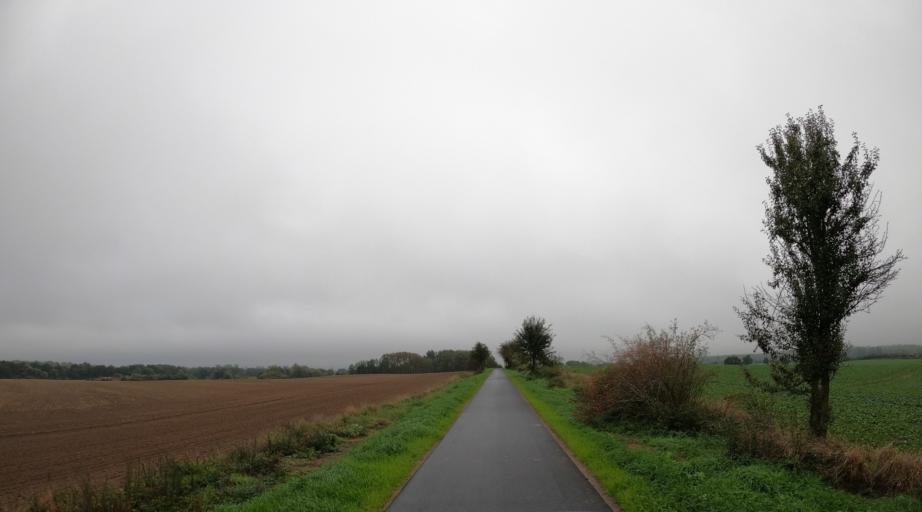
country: PL
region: West Pomeranian Voivodeship
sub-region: Powiat mysliborski
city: Mysliborz
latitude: 52.9232
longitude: 14.7367
